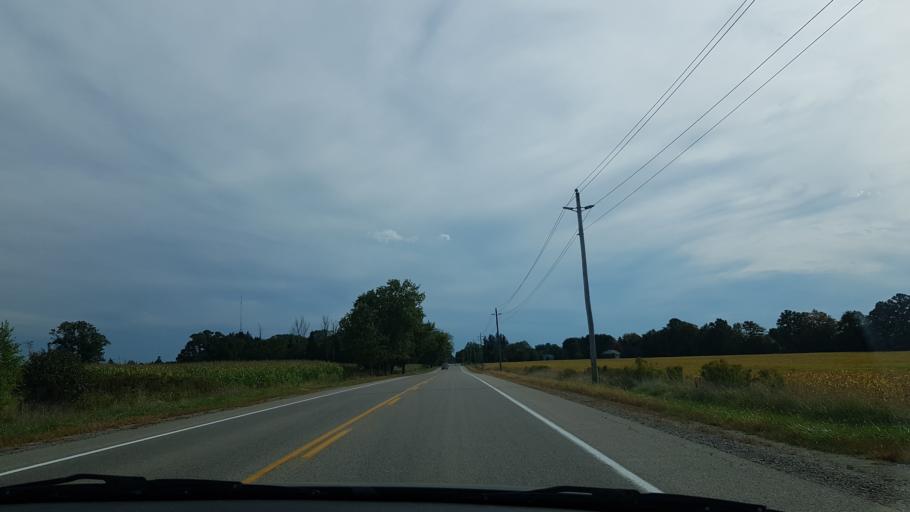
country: CA
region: Ontario
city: Delaware
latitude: 42.9891
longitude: -81.3904
